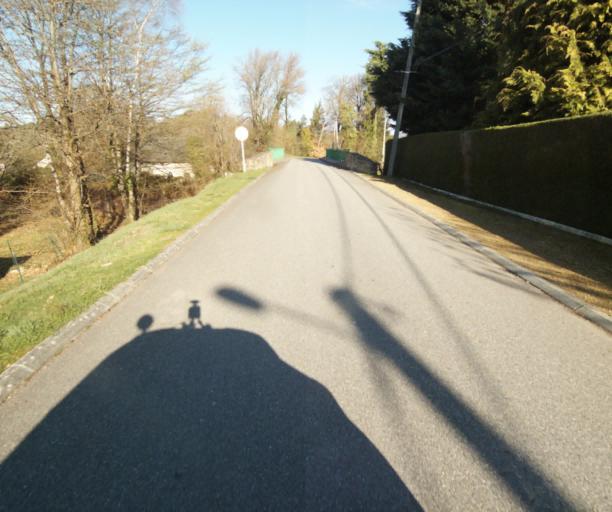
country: FR
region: Limousin
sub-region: Departement de la Correze
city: Correze
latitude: 45.3278
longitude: 1.8788
